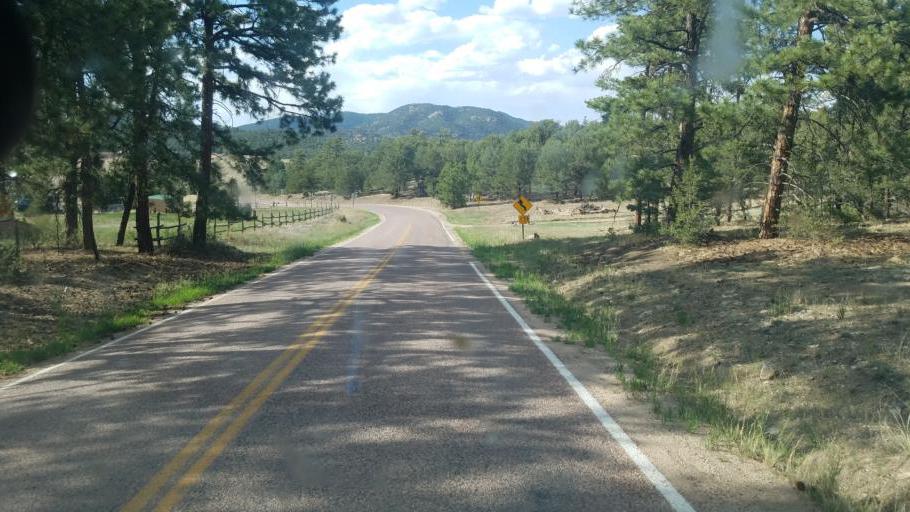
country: US
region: Colorado
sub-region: Custer County
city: Westcliffe
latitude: 38.3484
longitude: -105.4810
